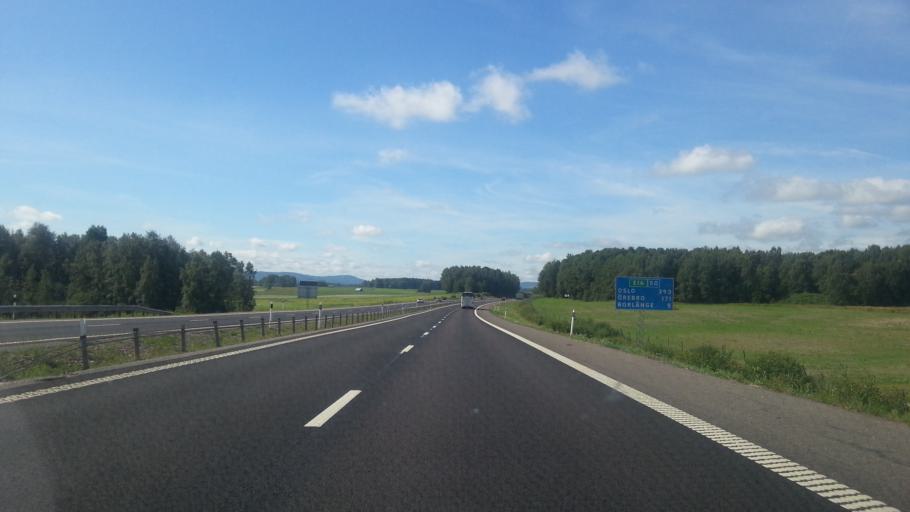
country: SE
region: Dalarna
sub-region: Borlange Kommun
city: Ornas
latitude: 60.4998
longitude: 15.5141
